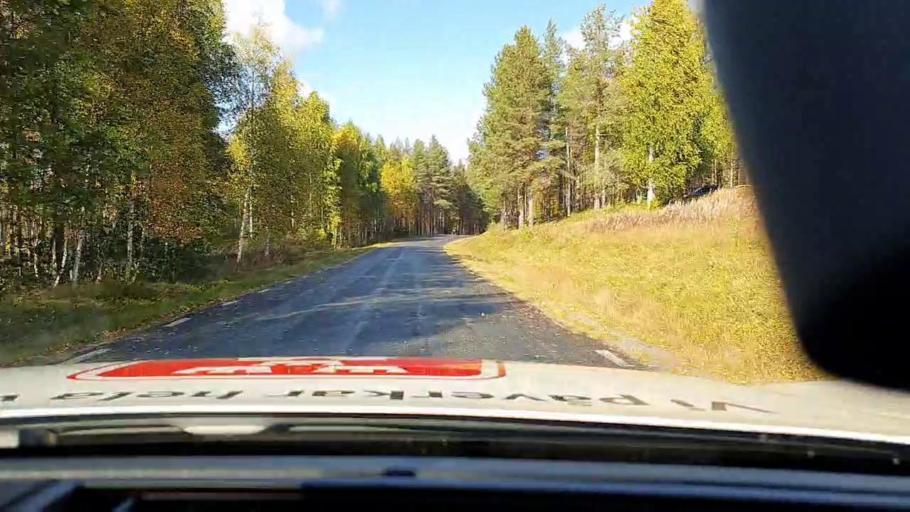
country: SE
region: Vaesterbotten
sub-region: Skelleftea Kommun
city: Langsele
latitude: 65.0150
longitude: 20.0786
